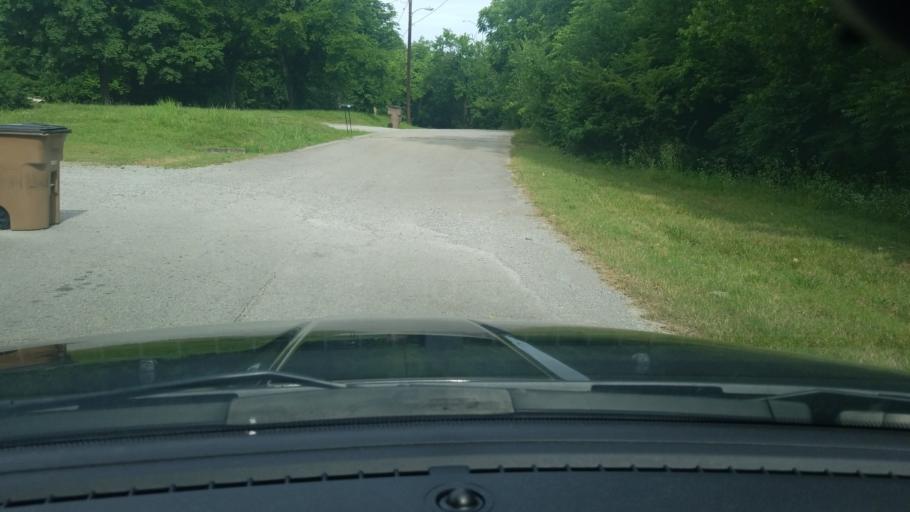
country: US
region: Tennessee
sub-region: Davidson County
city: Nashville
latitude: 36.2331
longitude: -86.7828
